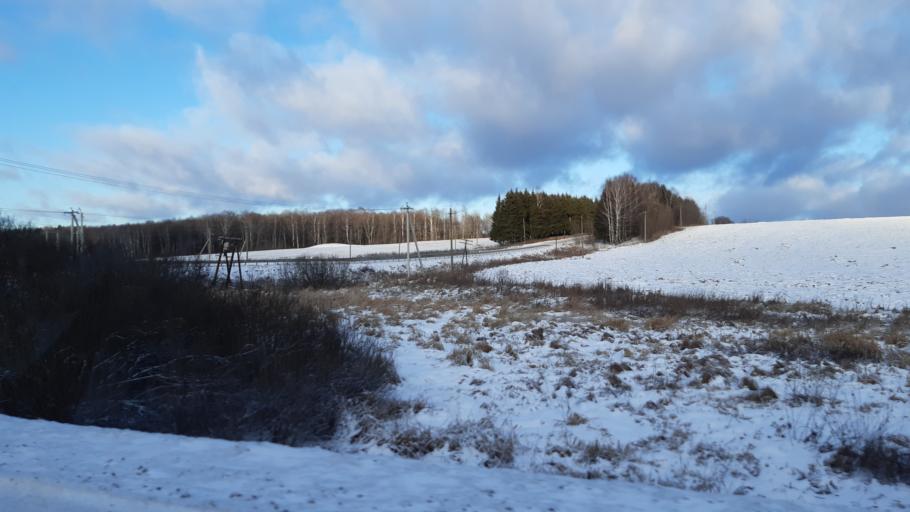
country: RU
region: Moskovskaya
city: Svatkovo
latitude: 56.3117
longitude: 38.3164
